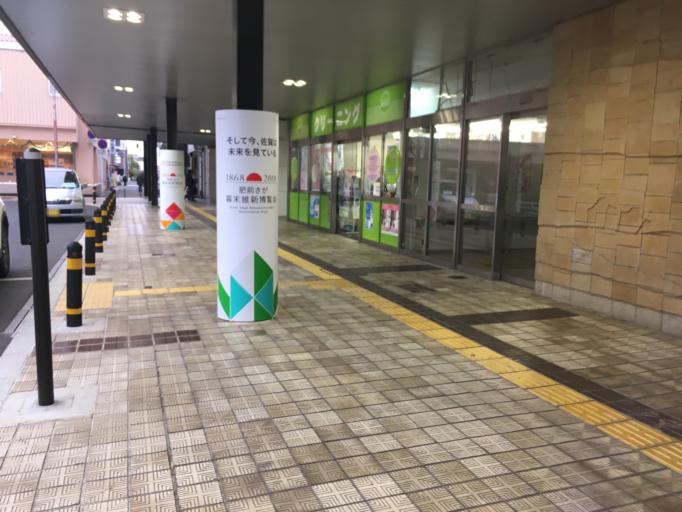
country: JP
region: Saga Prefecture
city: Saga-shi
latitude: 33.2638
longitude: 130.2974
